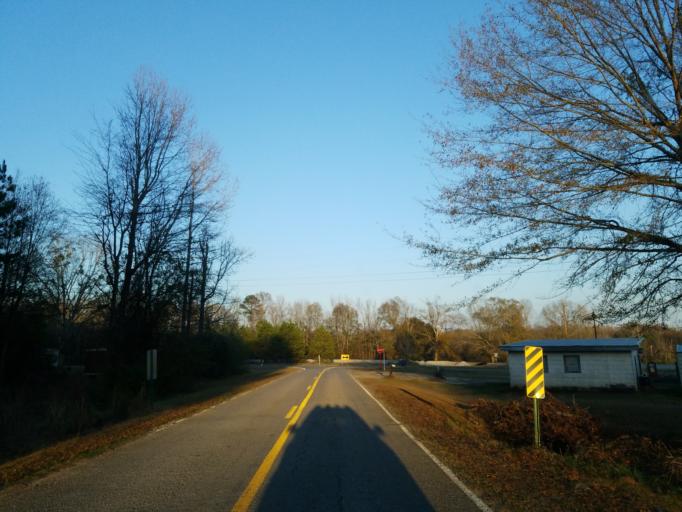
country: US
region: Mississippi
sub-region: Lauderdale County
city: Meridian
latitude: 32.2709
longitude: -88.7701
